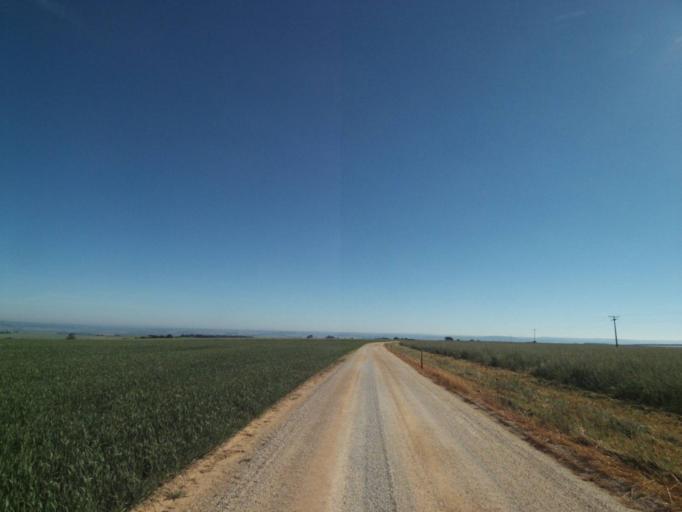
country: BR
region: Parana
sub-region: Tibagi
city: Tibagi
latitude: -24.5328
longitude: -50.3074
